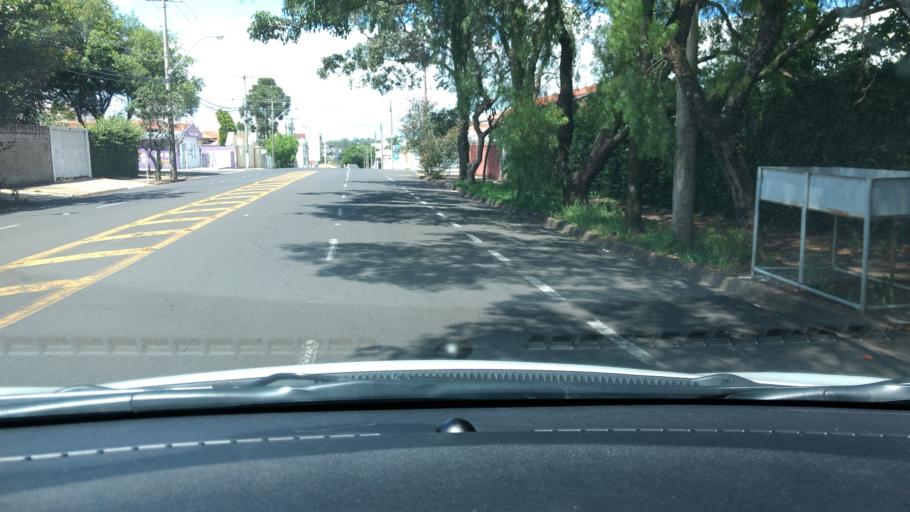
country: BR
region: Sao Paulo
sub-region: Botucatu
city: Botucatu
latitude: -22.8628
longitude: -48.4463
